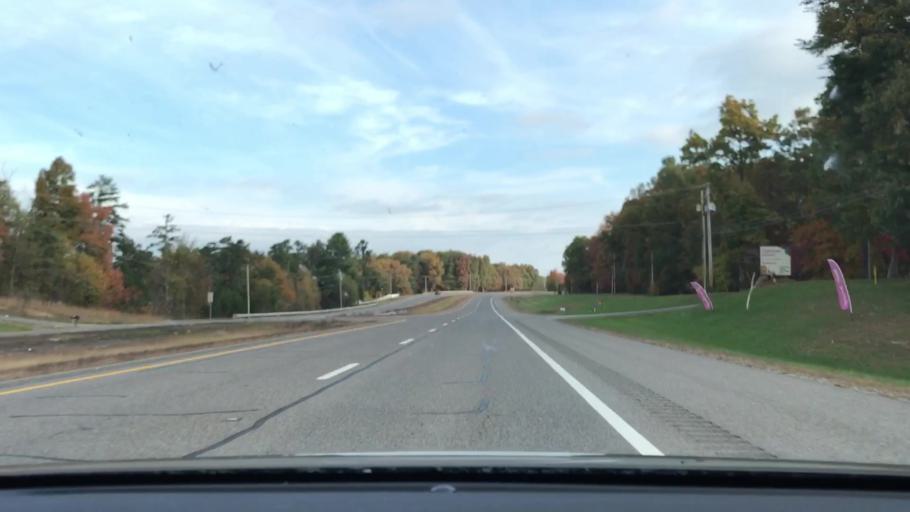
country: US
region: Tennessee
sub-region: Fentress County
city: Jamestown
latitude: 36.3769
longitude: -84.9434
